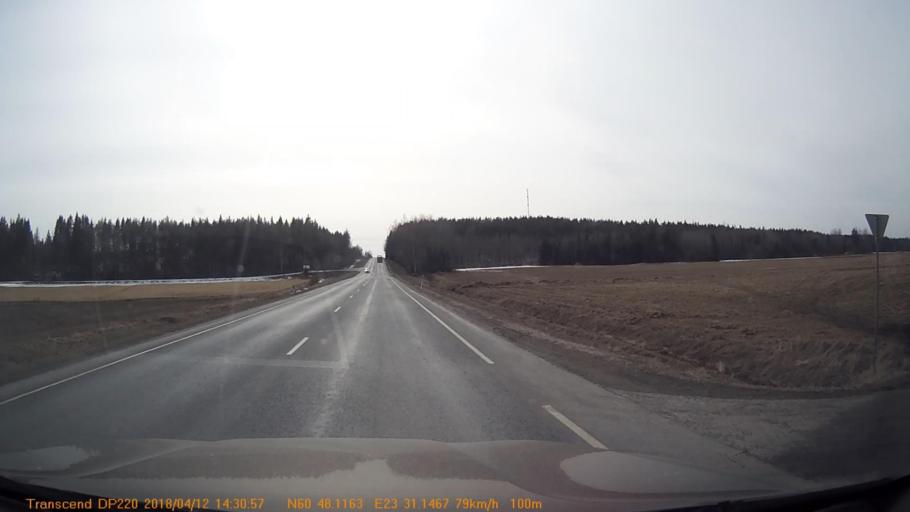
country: FI
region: Haeme
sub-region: Forssa
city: Jokioinen
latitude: 60.8016
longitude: 23.5184
